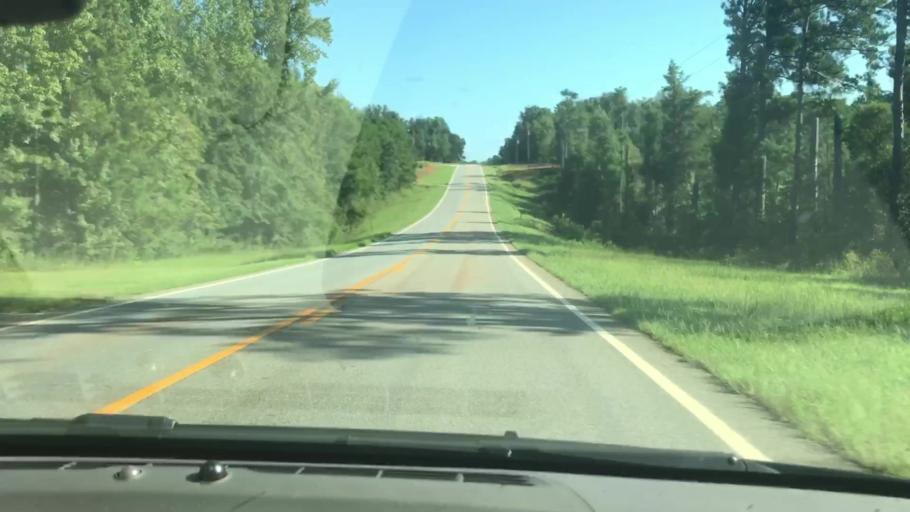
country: US
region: Georgia
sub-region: Quitman County
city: Georgetown
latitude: 31.8528
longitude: -85.0718
